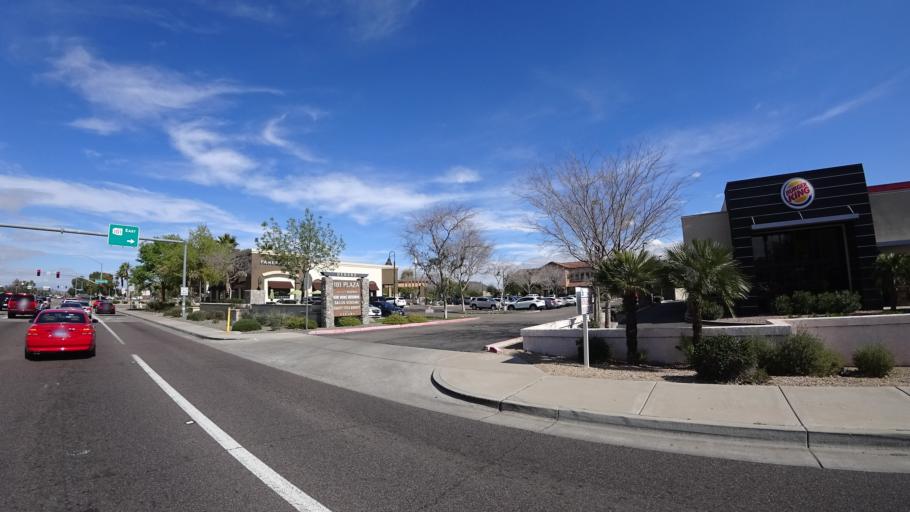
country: US
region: Arizona
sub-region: Maricopa County
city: Peoria
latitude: 33.6666
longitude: -112.2029
